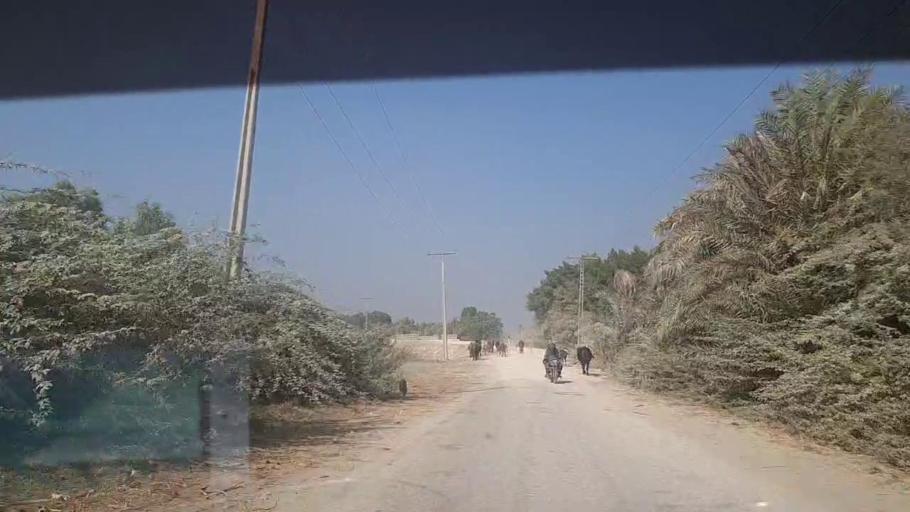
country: PK
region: Sindh
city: Kot Diji
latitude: 27.3575
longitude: 68.7104
